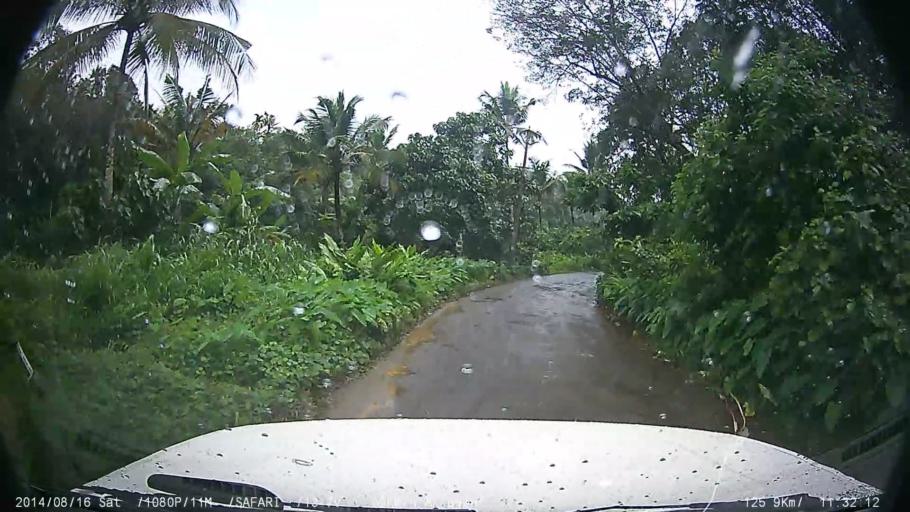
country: IN
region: Kerala
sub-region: Kottayam
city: Palackattumala
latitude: 9.7717
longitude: 76.5607
